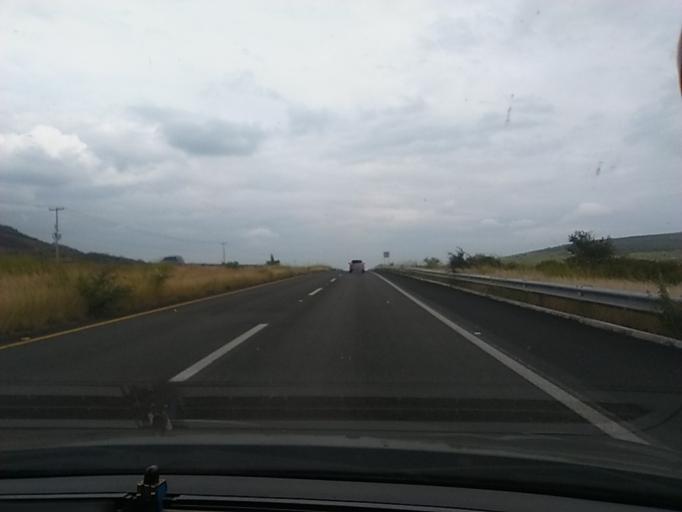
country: MX
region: Michoacan
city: Ecuandureo
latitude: 20.1743
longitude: -102.1735
